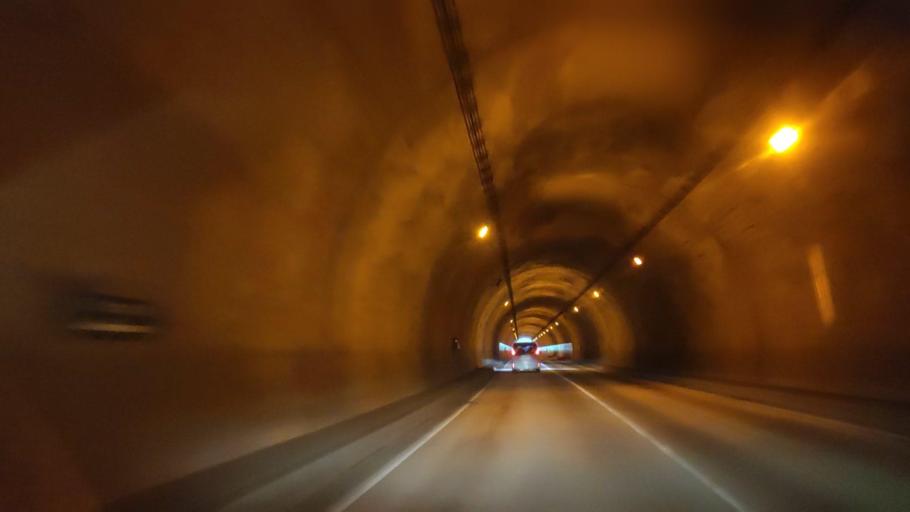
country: JP
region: Hokkaido
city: Shimo-furano
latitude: 43.3408
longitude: 142.2715
